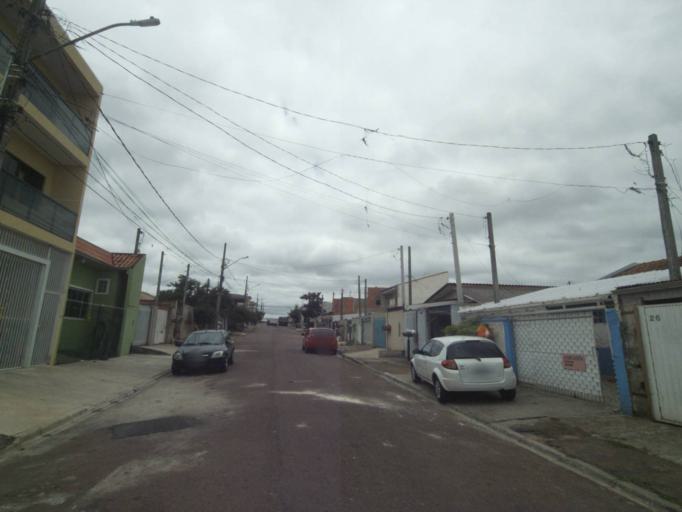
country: BR
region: Parana
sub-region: Sao Jose Dos Pinhais
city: Sao Jose dos Pinhais
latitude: -25.5574
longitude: -49.2633
